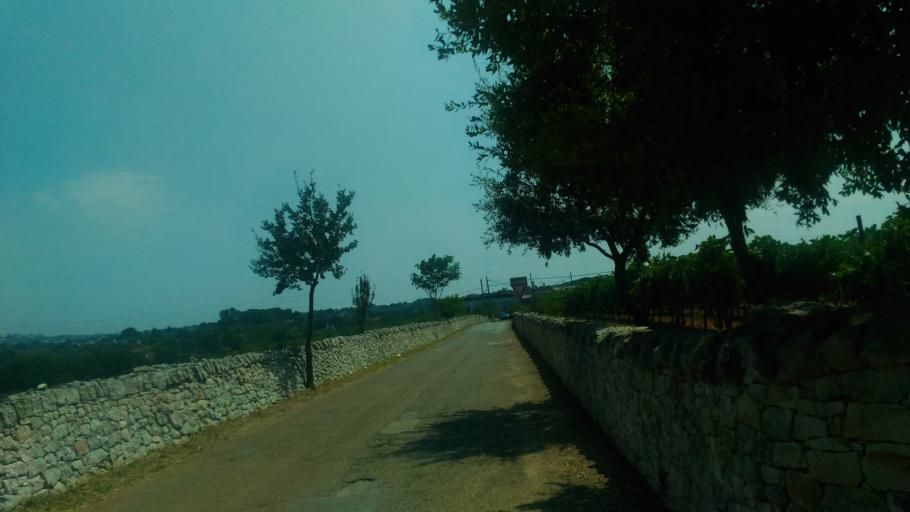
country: IT
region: Apulia
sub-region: Provincia di Brindisi
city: Cisternino
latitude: 40.7450
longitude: 17.3789
